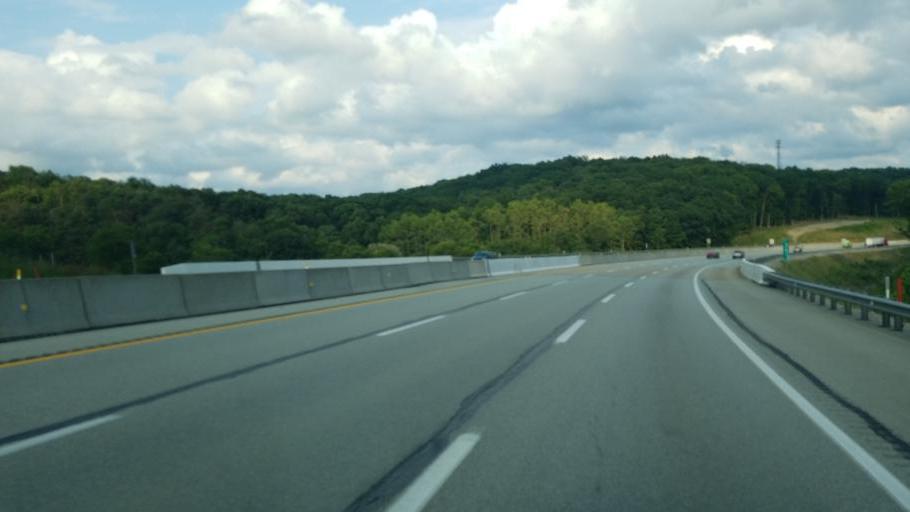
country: US
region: Pennsylvania
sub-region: Allegheny County
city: Gibsonia
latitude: 40.6403
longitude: -79.9980
